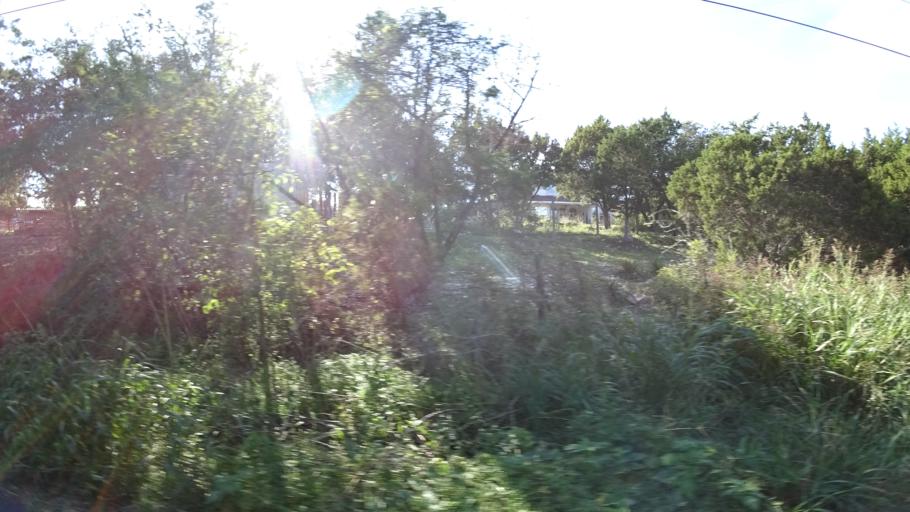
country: US
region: Texas
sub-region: Travis County
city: Bee Cave
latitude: 30.2366
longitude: -97.9385
